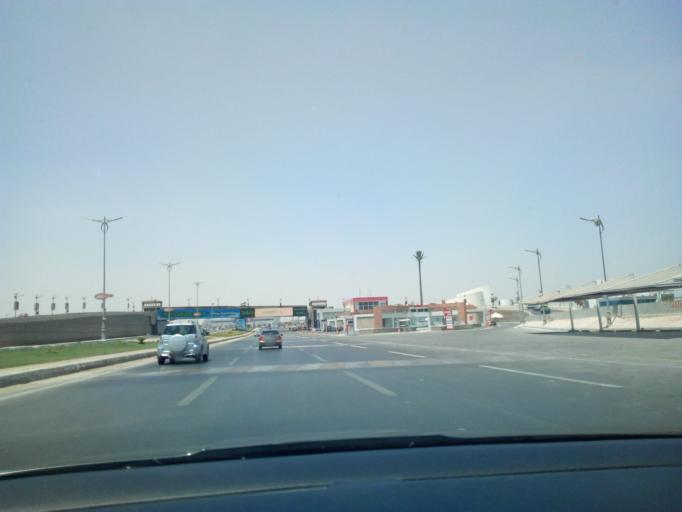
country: EG
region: Al Jizah
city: Awsim
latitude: 30.0672
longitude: 31.0184
